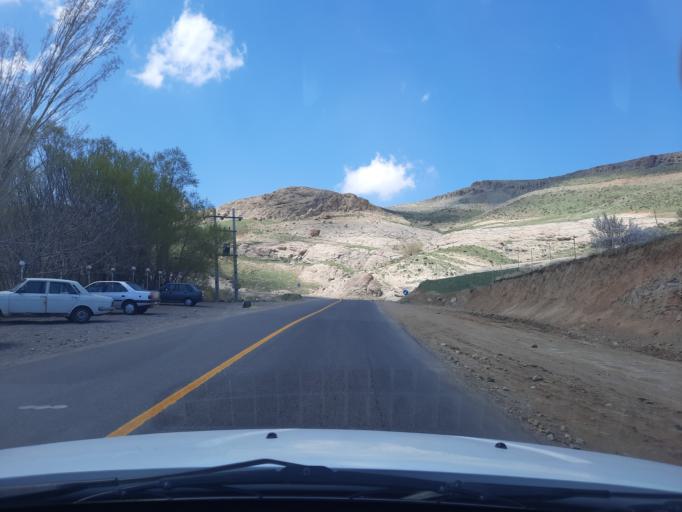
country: IR
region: Qazvin
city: Qazvin
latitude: 36.3807
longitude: 50.2092
